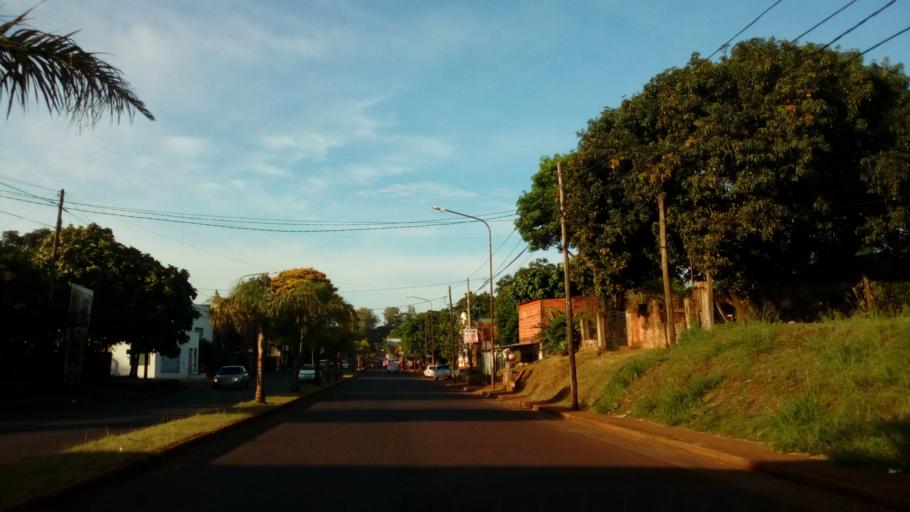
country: AR
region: Misiones
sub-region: Departamento de Capital
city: Posadas
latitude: -27.4013
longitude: -55.9212
